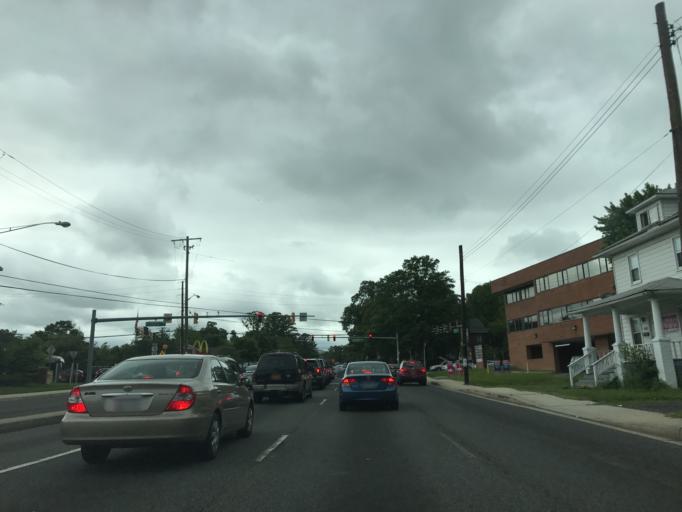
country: US
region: Maryland
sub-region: Prince George's County
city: Riverdale Park
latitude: 38.9644
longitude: -76.9382
